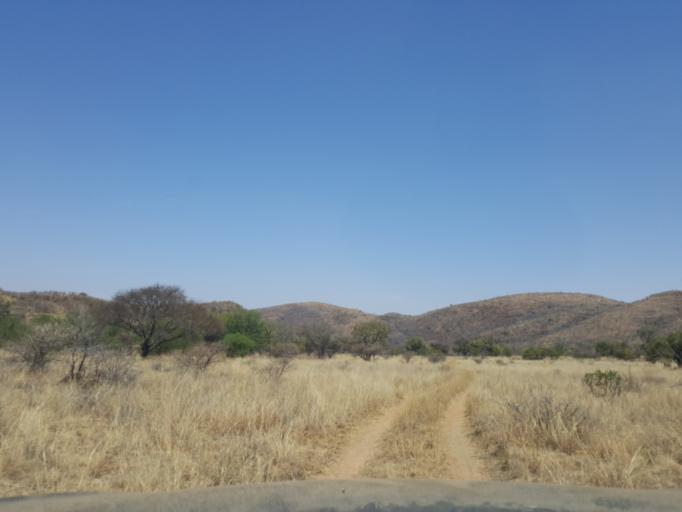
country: BW
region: South East
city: Lobatse
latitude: -25.1376
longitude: 25.6720
